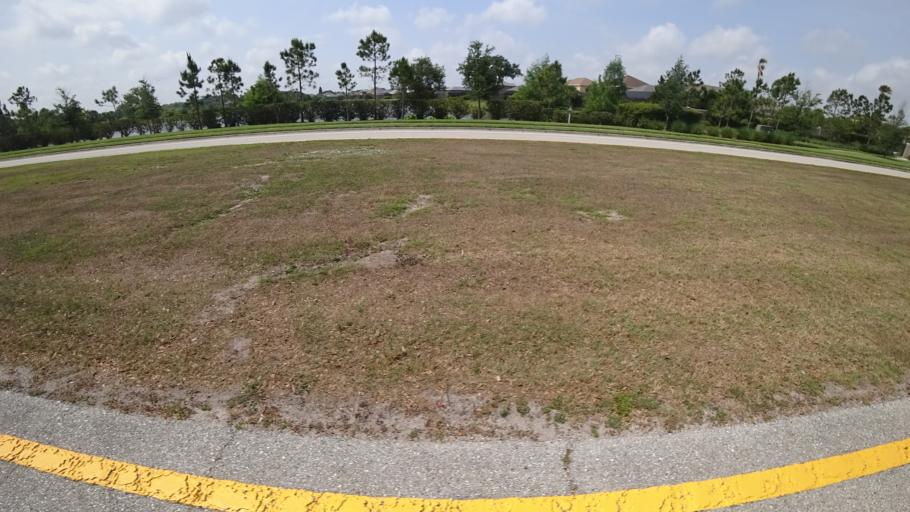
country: US
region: Florida
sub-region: Sarasota County
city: North Sarasota
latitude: 27.4188
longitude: -82.5113
